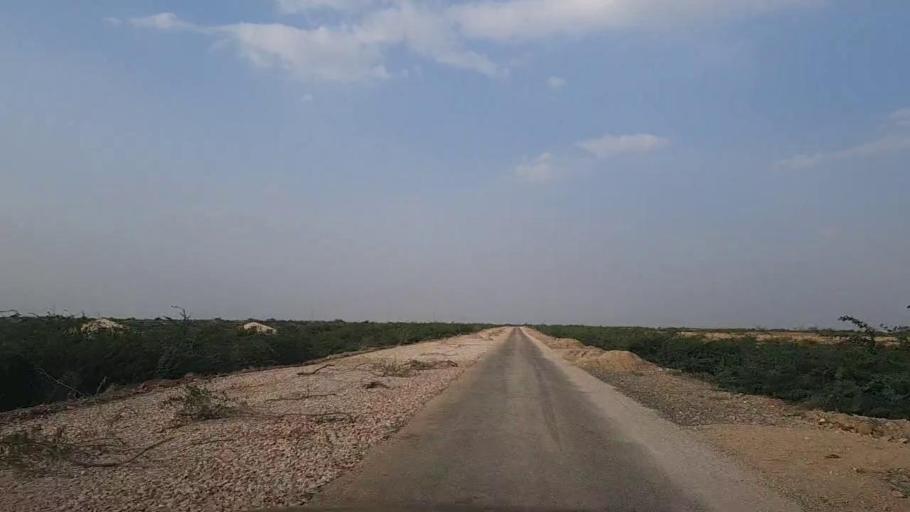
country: PK
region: Sindh
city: Gharo
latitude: 24.8421
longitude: 67.7460
